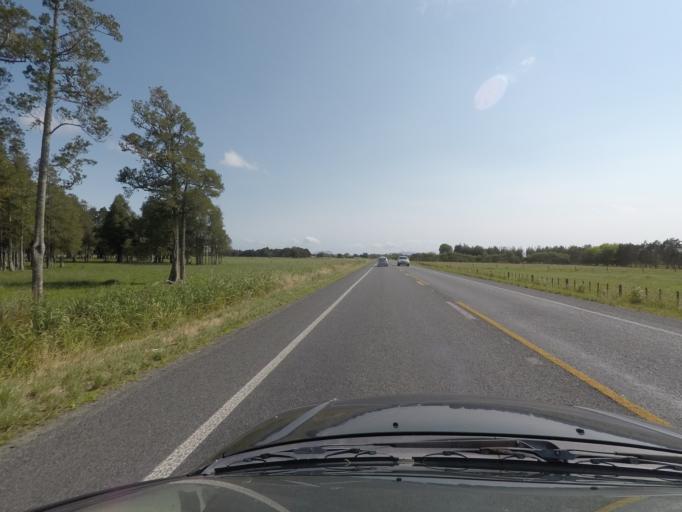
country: NZ
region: Northland
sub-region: Whangarei
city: Ruakaka
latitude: -35.9829
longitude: 174.4317
